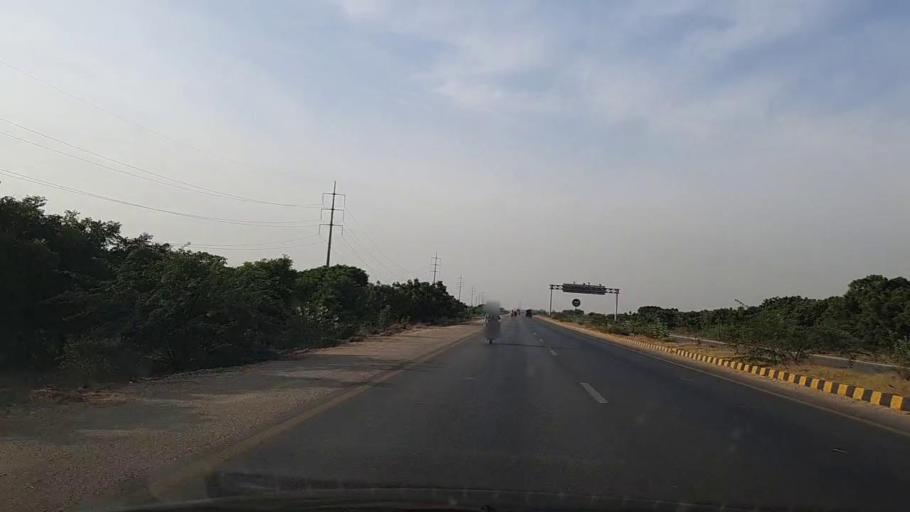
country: PK
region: Sindh
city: Gharo
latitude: 24.7701
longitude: 67.5478
